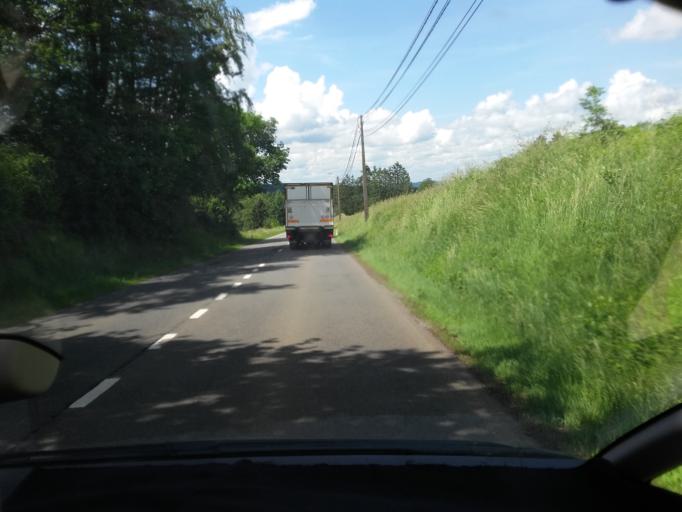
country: BE
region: Wallonia
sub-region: Province de Namur
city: Rochefort
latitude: 50.1384
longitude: 5.2251
